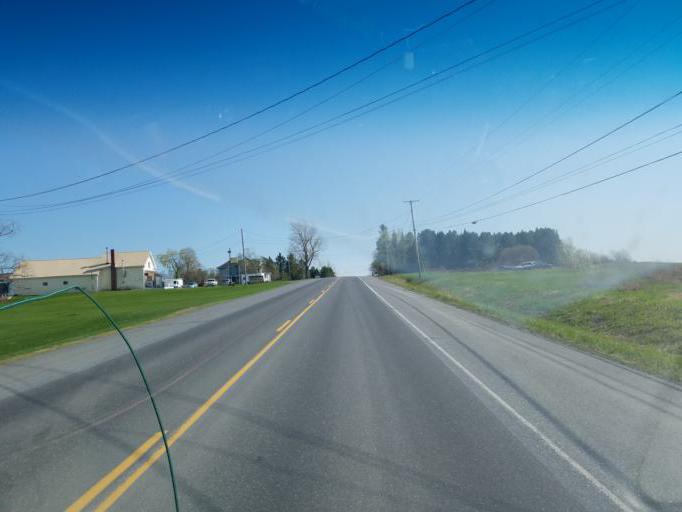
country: US
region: Maine
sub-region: Aroostook County
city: Caribou
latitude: 46.7955
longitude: -67.9915
